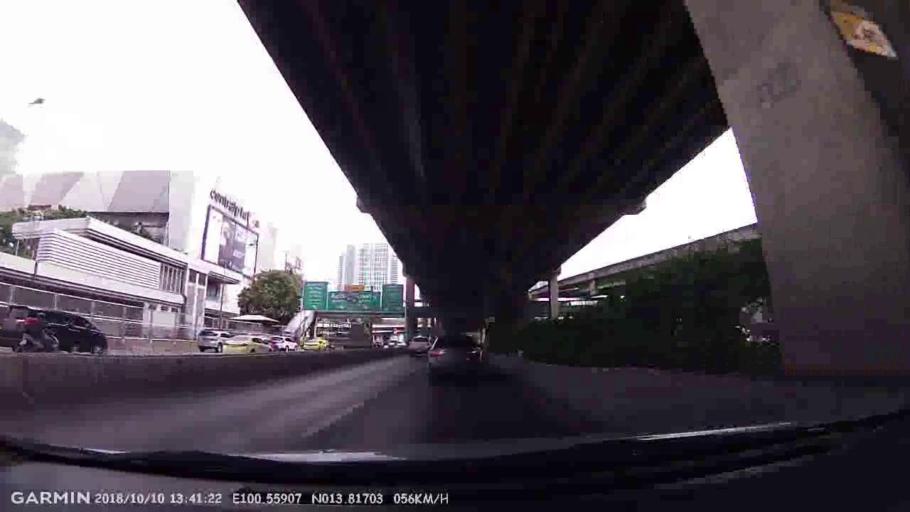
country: TH
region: Bangkok
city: Chatuchak
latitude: 13.8169
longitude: 100.5591
